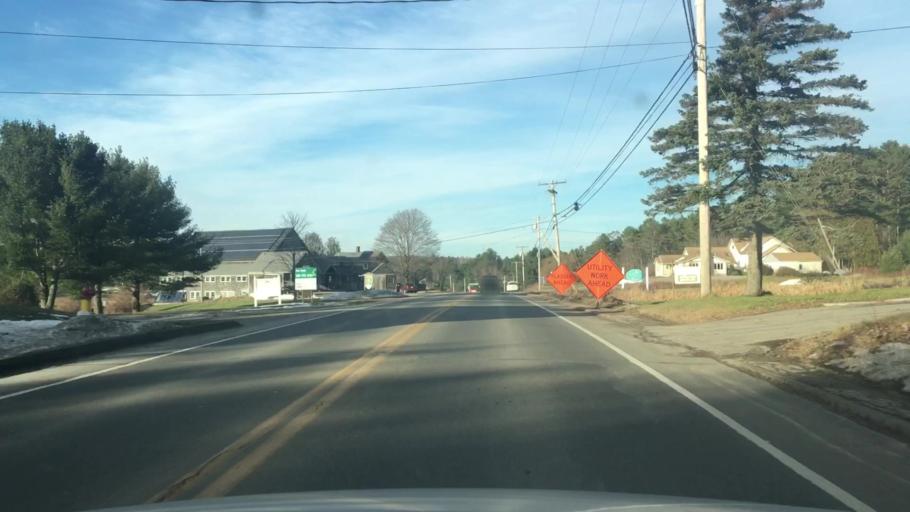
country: US
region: Maine
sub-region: Lincoln County
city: Wiscasset
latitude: 44.0139
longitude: -69.6679
